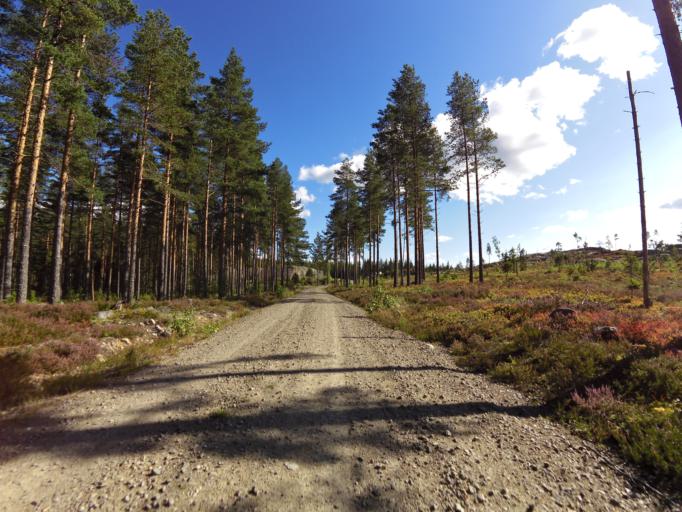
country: SE
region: Gaevleborg
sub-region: Ockelbo Kommun
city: Ockelbo
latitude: 60.8261
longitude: 16.7588
